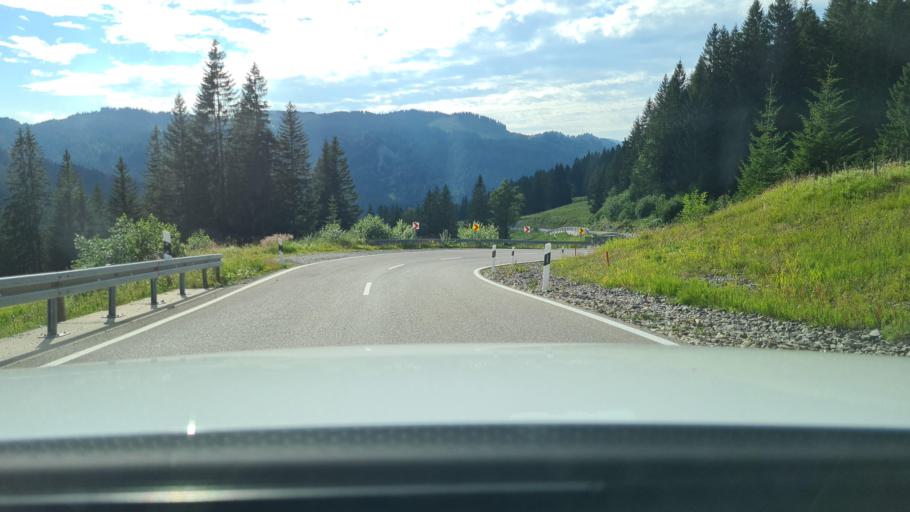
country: DE
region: Bavaria
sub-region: Swabia
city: Balderschwang
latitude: 47.4335
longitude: 10.1614
